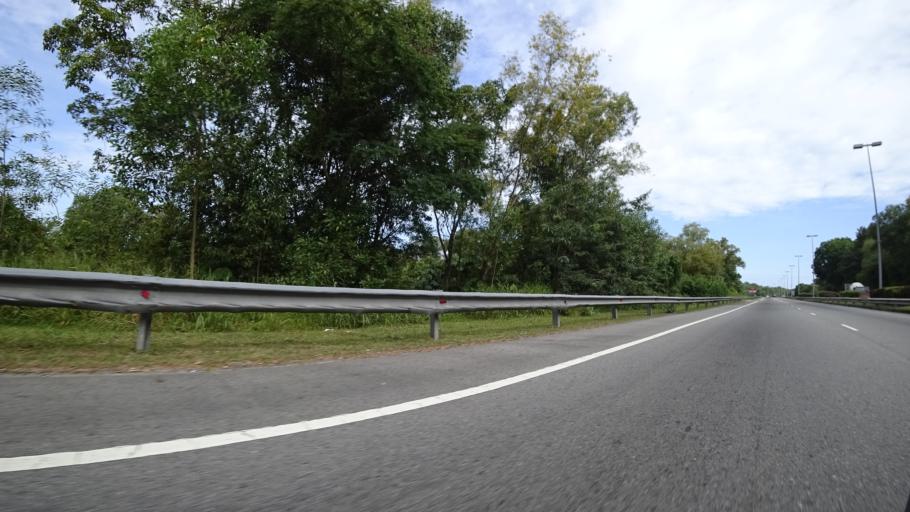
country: BN
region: Brunei and Muara
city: Bandar Seri Begawan
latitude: 4.9273
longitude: 114.9114
